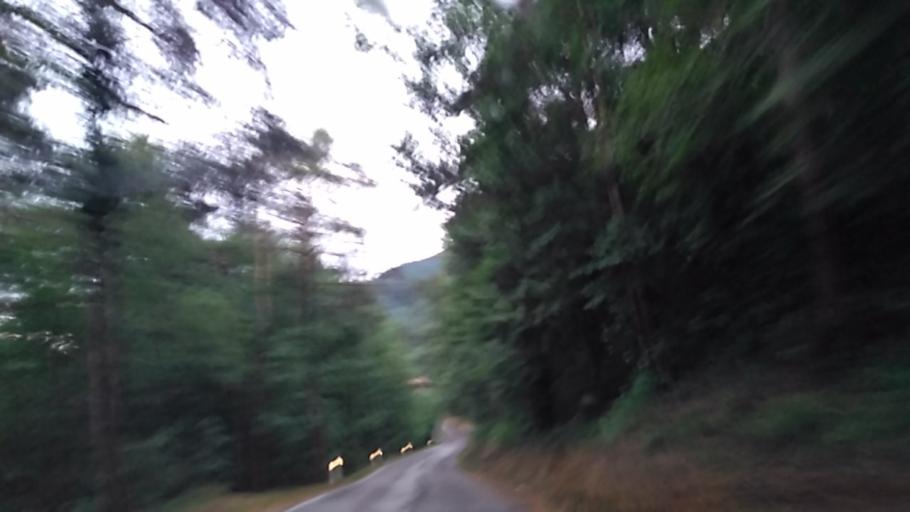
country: IT
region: Lombardy
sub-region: Provincia di Brescia
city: Gardola
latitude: 45.7675
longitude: 10.7177
